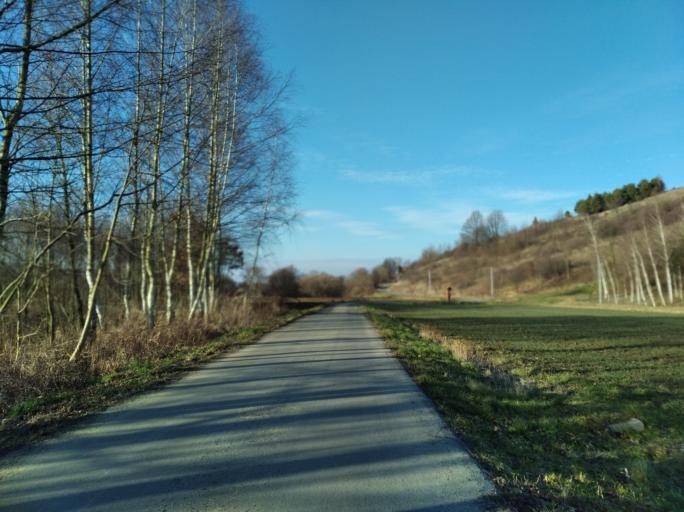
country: PL
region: Subcarpathian Voivodeship
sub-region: Powiat strzyzowski
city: Strzyzow
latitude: 49.8249
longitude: 21.8345
